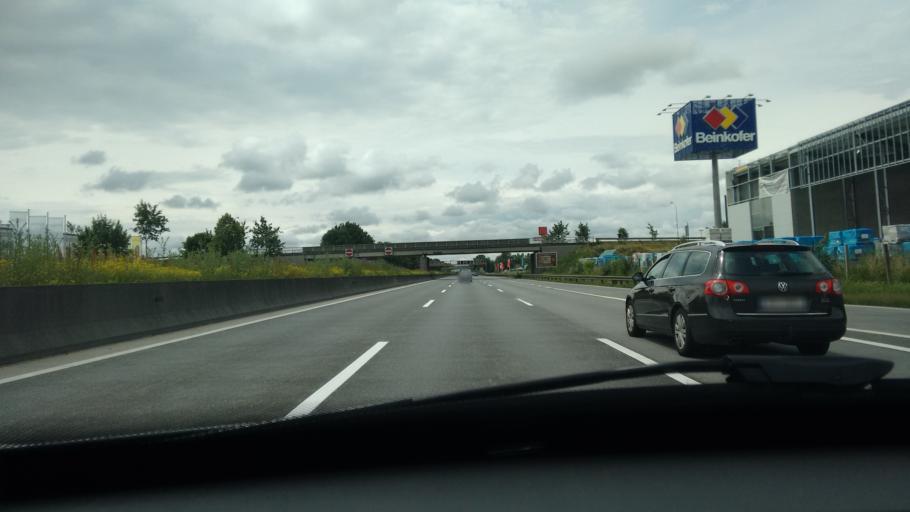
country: AT
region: Upper Austria
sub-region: Politischer Bezirk Linz-Land
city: Ansfelden
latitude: 48.2128
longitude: 14.2799
